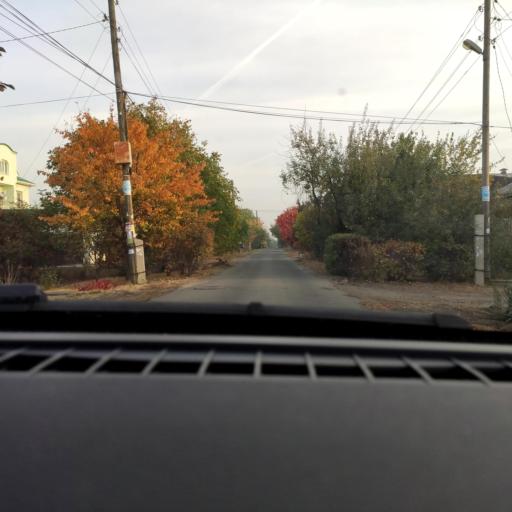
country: RU
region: Voronezj
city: Voronezh
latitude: 51.6629
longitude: 39.2629
